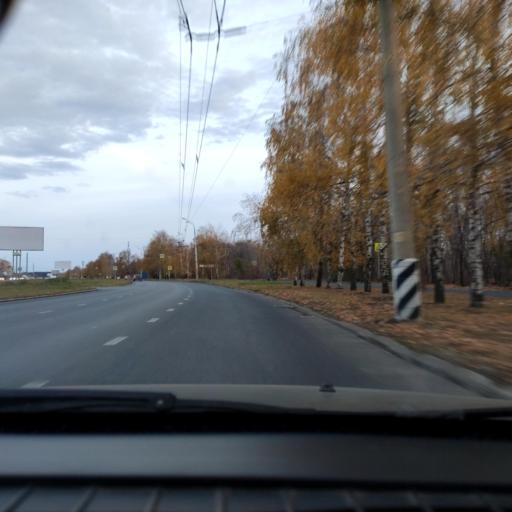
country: RU
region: Samara
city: Tol'yatti
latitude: 53.5004
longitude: 49.2662
